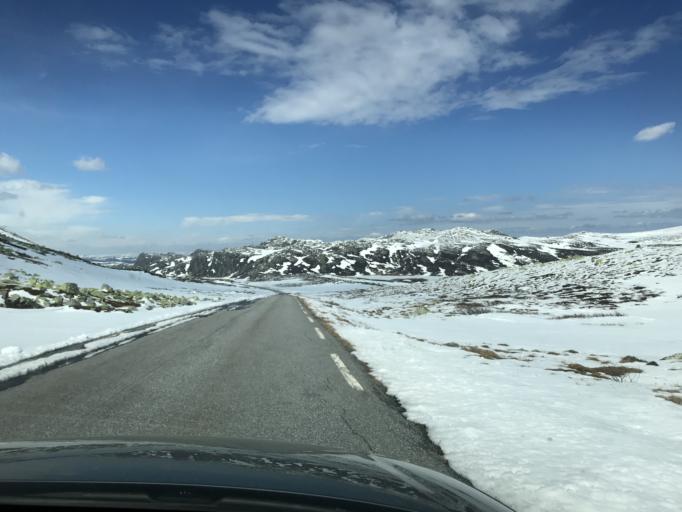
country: NO
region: Telemark
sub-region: Tinn
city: Rjukan
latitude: 59.8203
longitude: 8.7222
